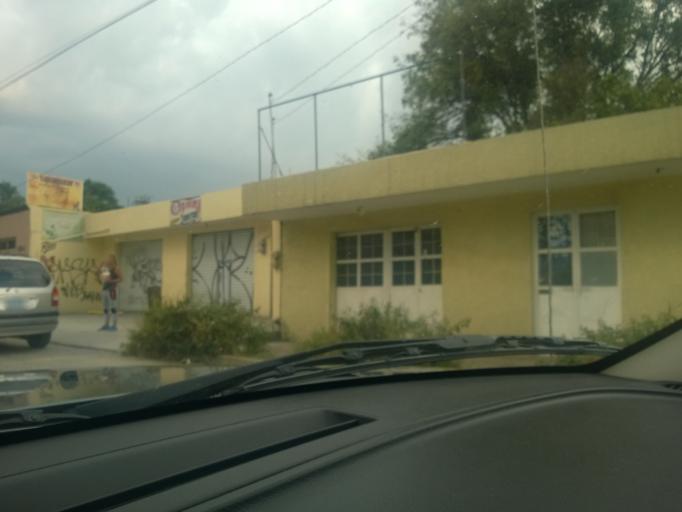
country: MX
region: Guanajuato
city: Leon
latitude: 21.1186
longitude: -101.6452
